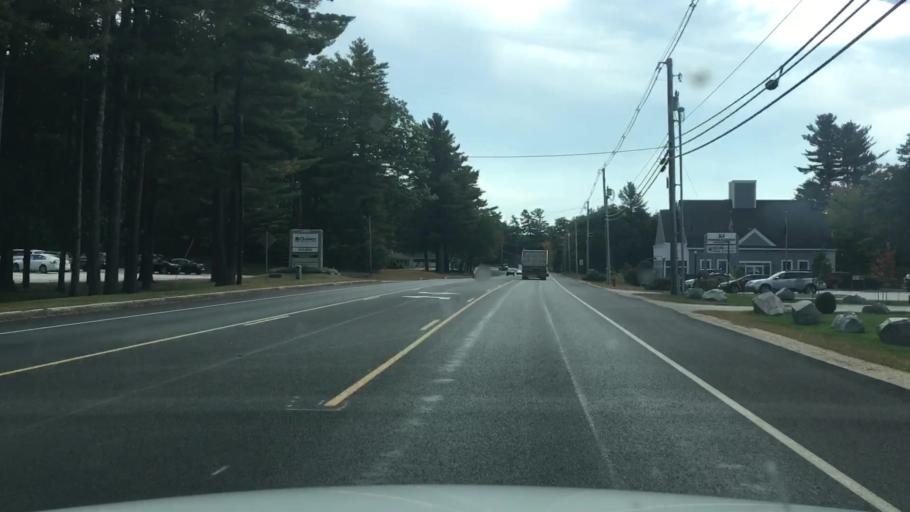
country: US
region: New Hampshire
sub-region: Carroll County
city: North Conway
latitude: 44.0663
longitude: -71.1427
